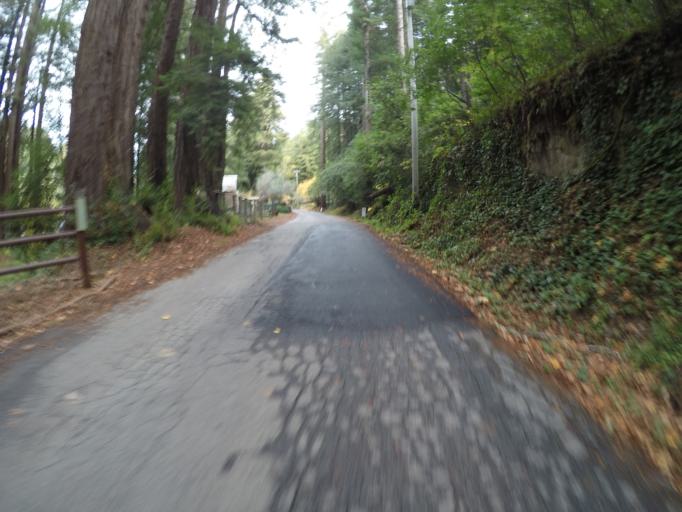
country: US
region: California
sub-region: Santa Cruz County
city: Scotts Valley
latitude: 37.0361
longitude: -121.9802
